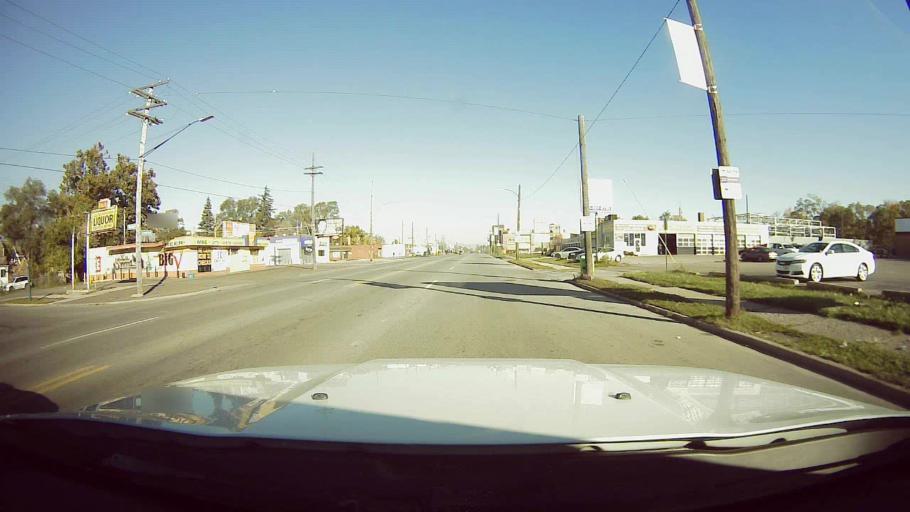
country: US
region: Michigan
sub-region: Wayne County
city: Dearborn
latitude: 42.3893
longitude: -83.1982
